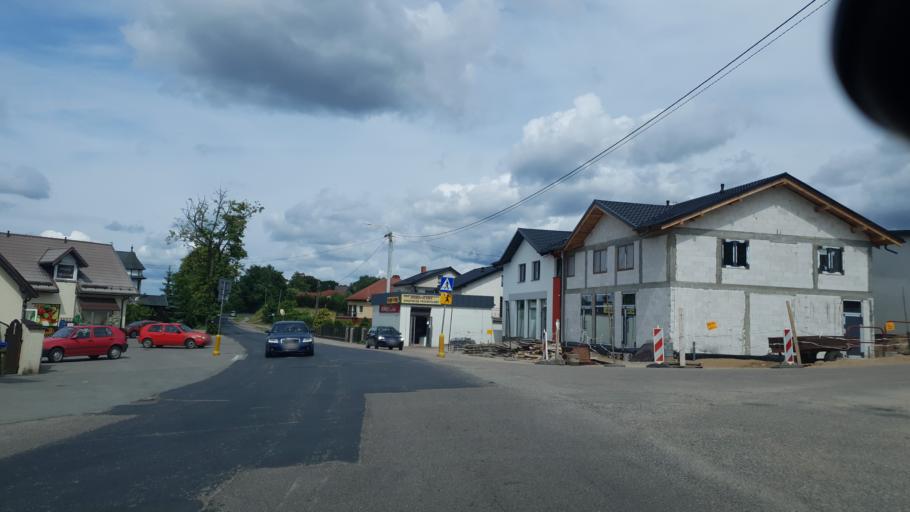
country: PL
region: Pomeranian Voivodeship
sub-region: Powiat kartuski
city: Chmielno
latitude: 54.2701
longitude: 18.0825
